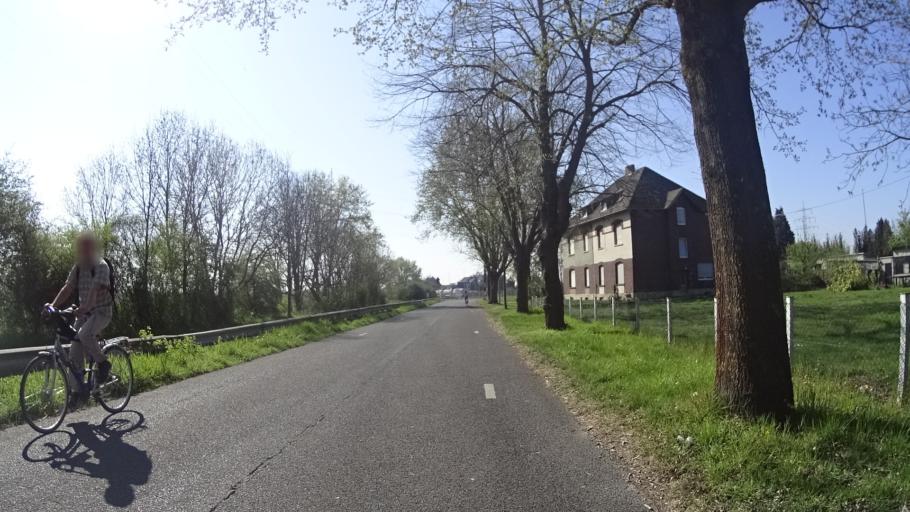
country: DE
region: North Rhine-Westphalia
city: Rheinberg
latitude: 51.5611
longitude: 6.5866
